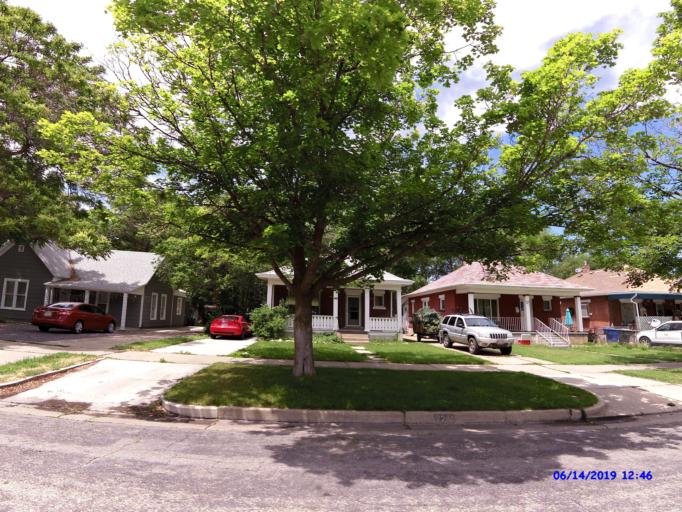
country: US
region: Utah
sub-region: Weber County
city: Ogden
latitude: 41.2258
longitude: -111.9564
